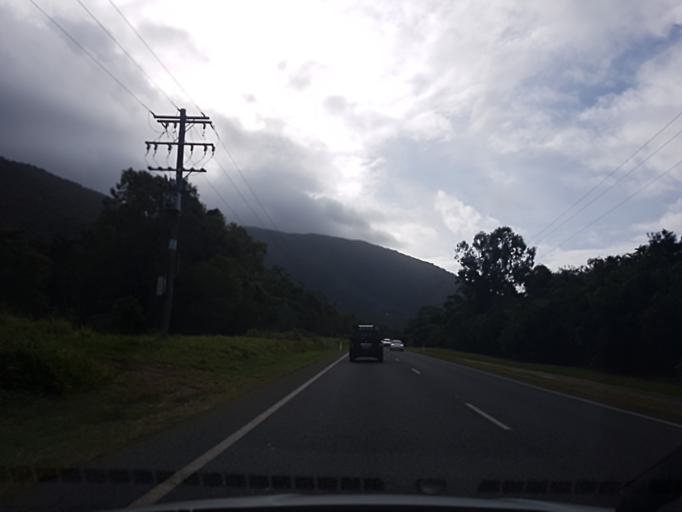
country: AU
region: Queensland
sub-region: Cairns
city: Palm Cove
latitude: -16.7621
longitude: 145.6659
